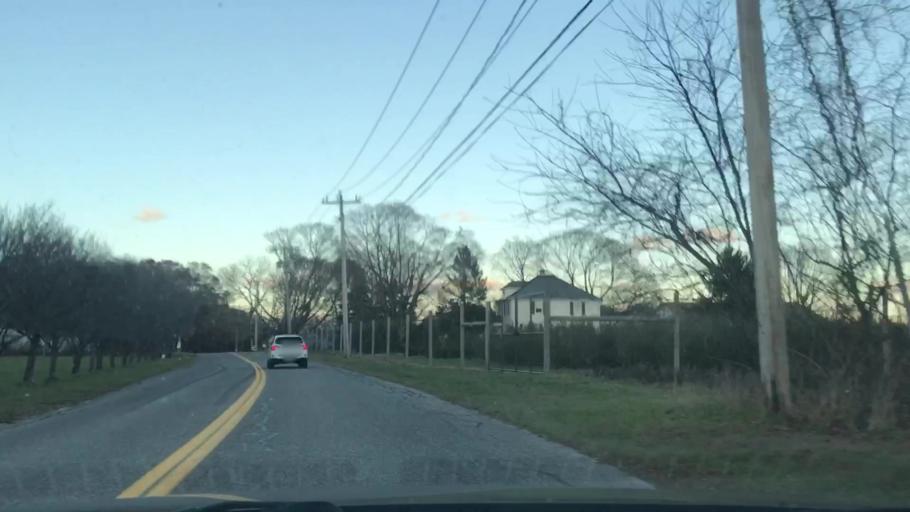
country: US
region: New York
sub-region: Suffolk County
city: Calverton
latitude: 40.9305
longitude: -72.7180
